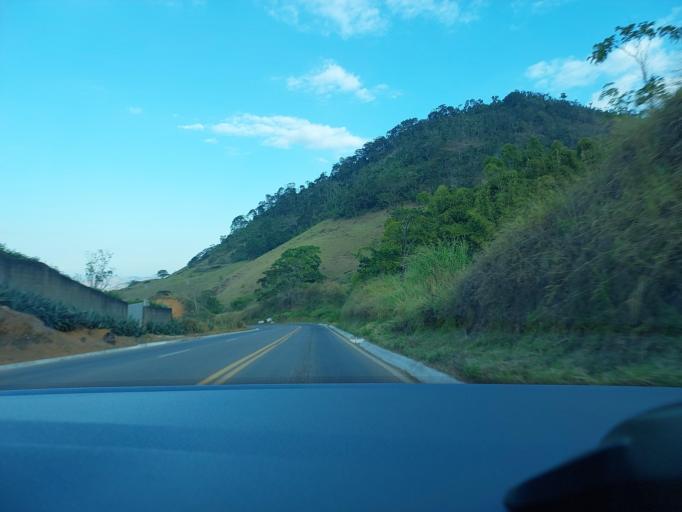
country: BR
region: Minas Gerais
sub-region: Muriae
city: Muriae
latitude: -21.0847
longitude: -42.4899
